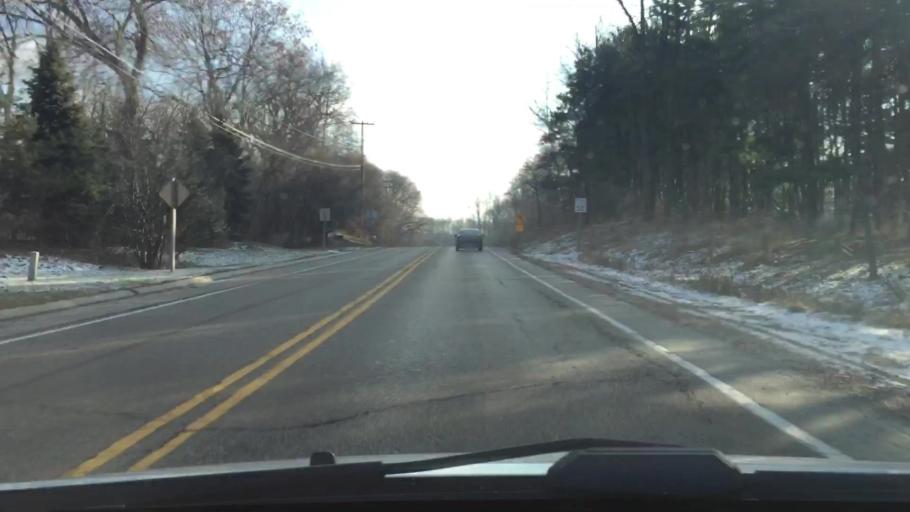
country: US
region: Wisconsin
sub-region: Waukesha County
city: Dousman
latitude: 43.0196
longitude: -88.4367
